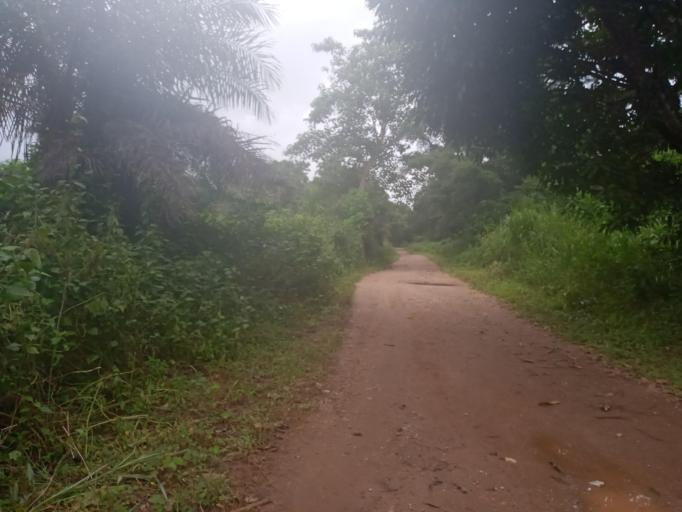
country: SL
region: Northern Province
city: Bumbuna
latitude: 8.9553
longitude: -11.7596
